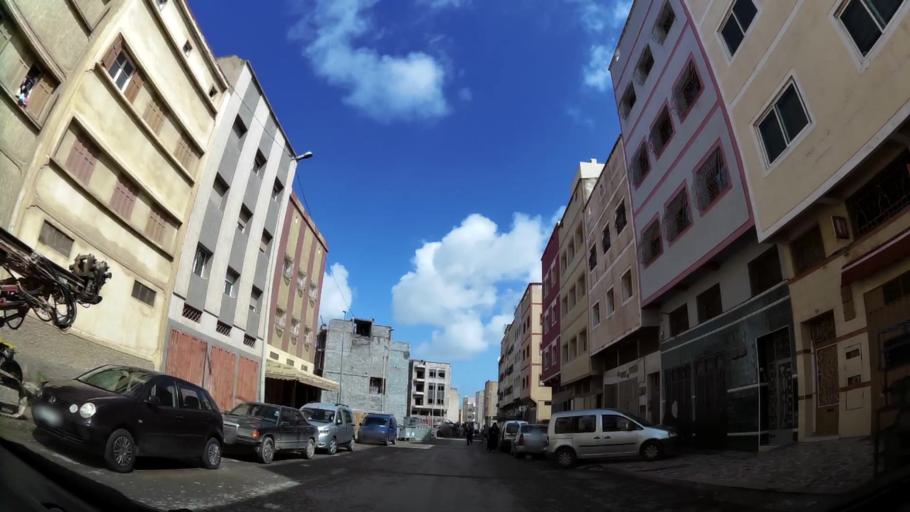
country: MA
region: Grand Casablanca
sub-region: Casablanca
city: Casablanca
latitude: 33.5364
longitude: -7.5786
